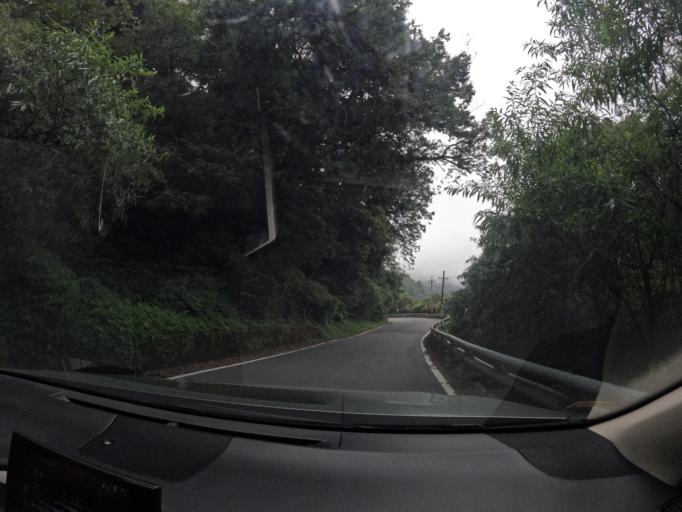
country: TW
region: Taiwan
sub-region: Taitung
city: Taitung
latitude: 23.2463
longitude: 120.9927
